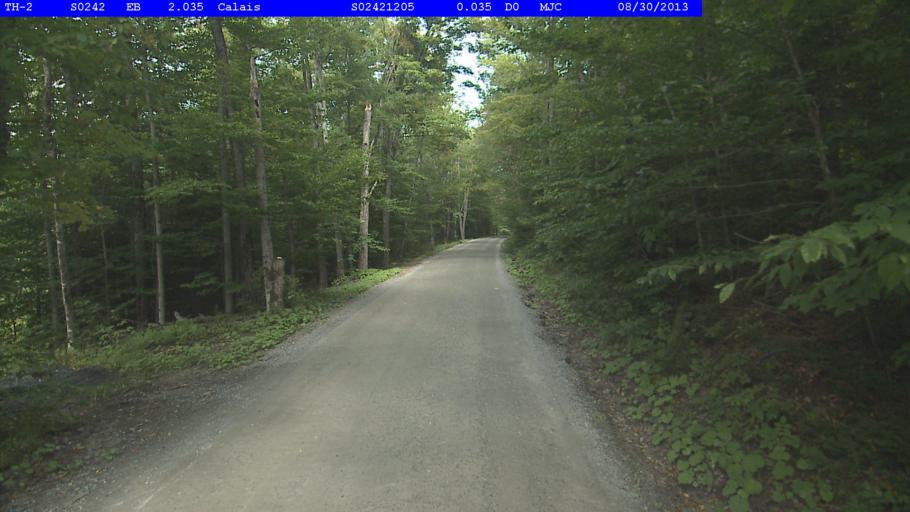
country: US
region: Vermont
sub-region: Washington County
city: Montpelier
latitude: 44.3882
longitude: -72.5192
